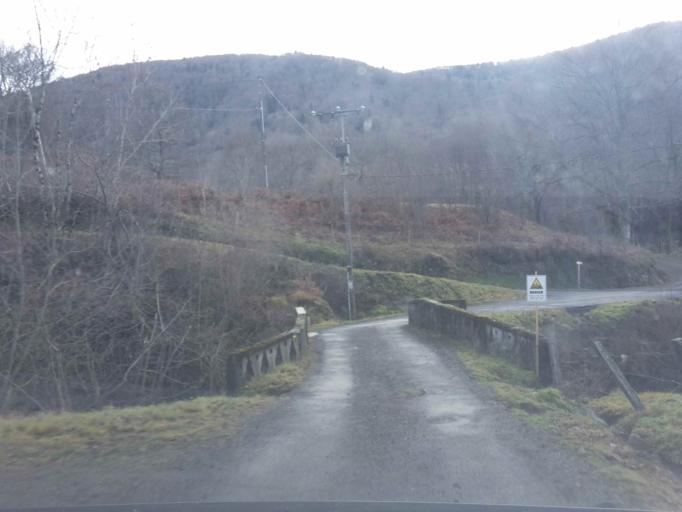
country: FR
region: Auvergne
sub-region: Departement du Cantal
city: Riom-es-Montagnes
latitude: 45.1852
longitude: 2.5711
